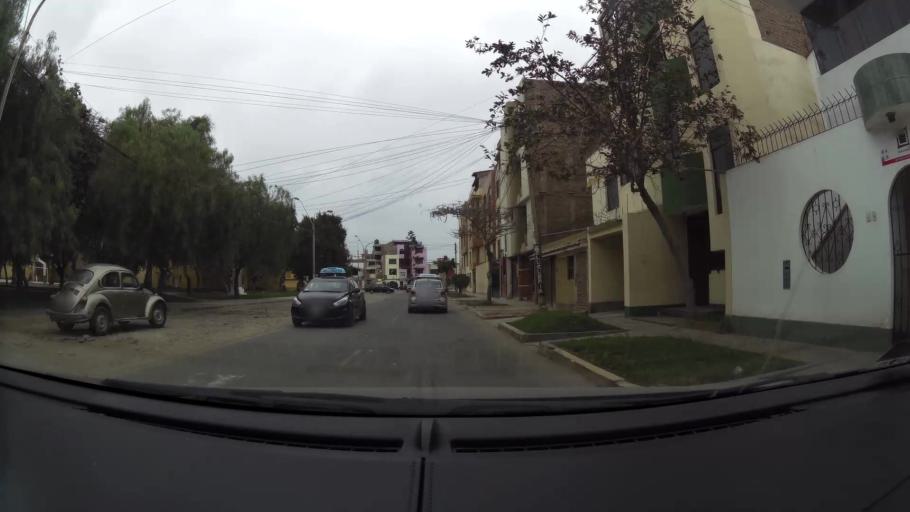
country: PE
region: La Libertad
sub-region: Provincia de Trujillo
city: Trujillo
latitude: -8.1208
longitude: -79.0427
